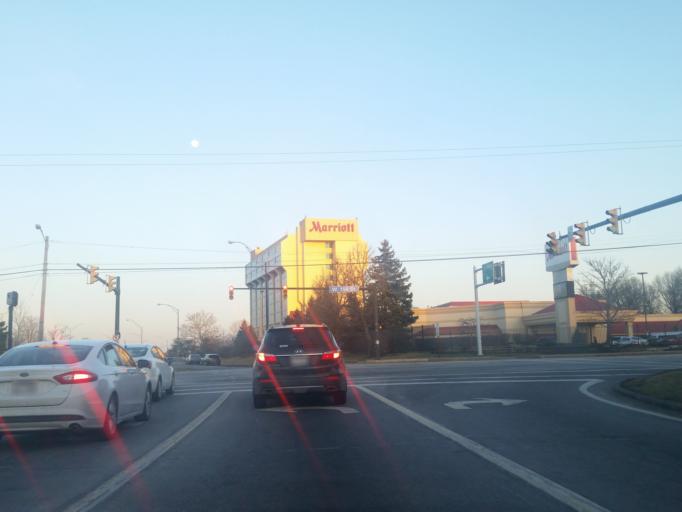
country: US
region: Ohio
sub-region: Cuyahoga County
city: Brook Park
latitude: 41.4381
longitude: -81.8017
